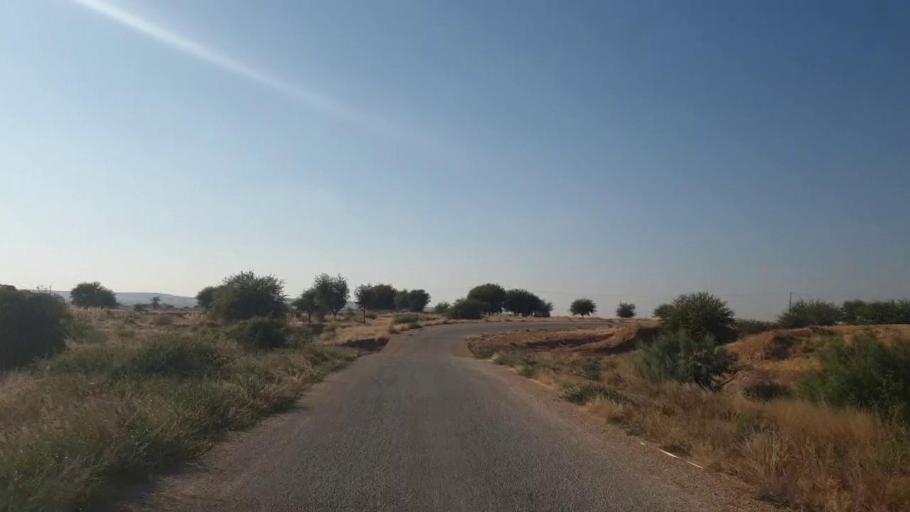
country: PK
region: Sindh
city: Malir Cantonment
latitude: 25.4059
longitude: 67.4682
